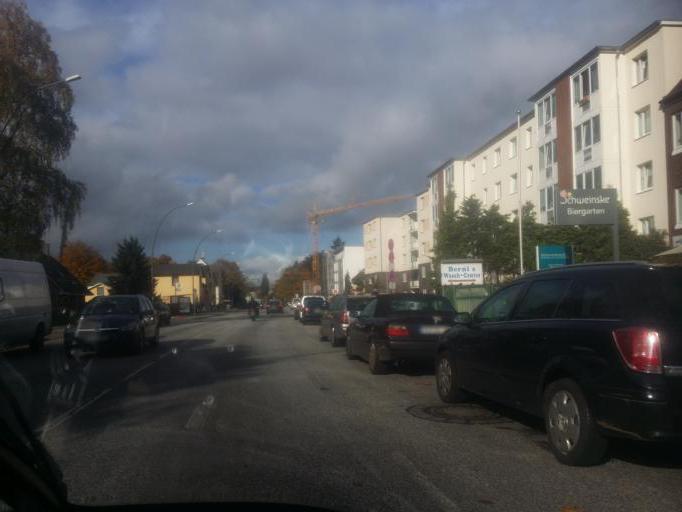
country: DE
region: Hamburg
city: Eidelstedt
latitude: 53.5925
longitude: 9.8712
